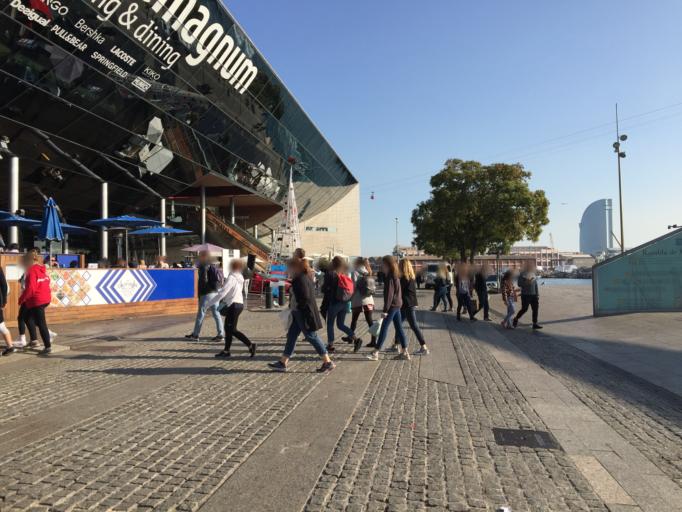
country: ES
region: Catalonia
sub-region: Provincia de Barcelona
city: Ciutat Vella
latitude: 41.3748
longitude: 2.1821
